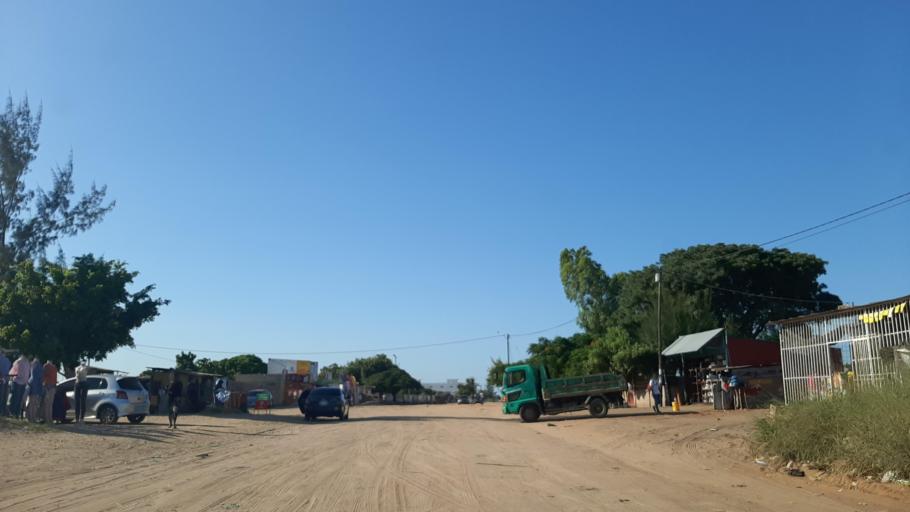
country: MZ
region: Maputo City
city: Maputo
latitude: -25.8092
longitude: 32.5462
